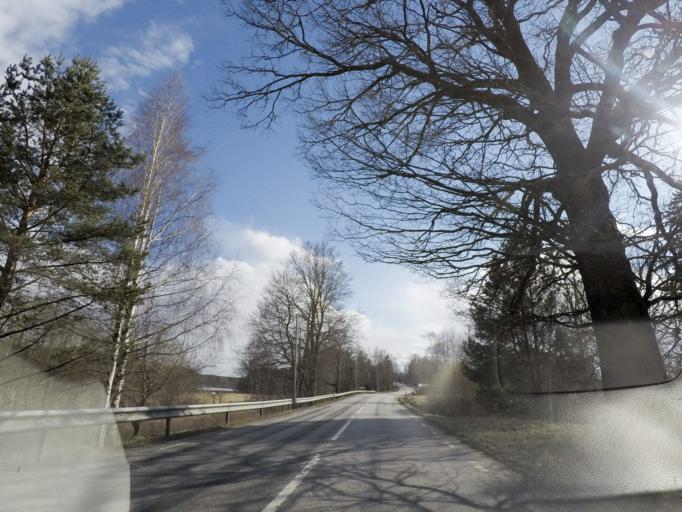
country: SE
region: Vaestmanland
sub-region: Surahammars Kommun
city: Surahammar
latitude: 59.6819
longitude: 16.1843
